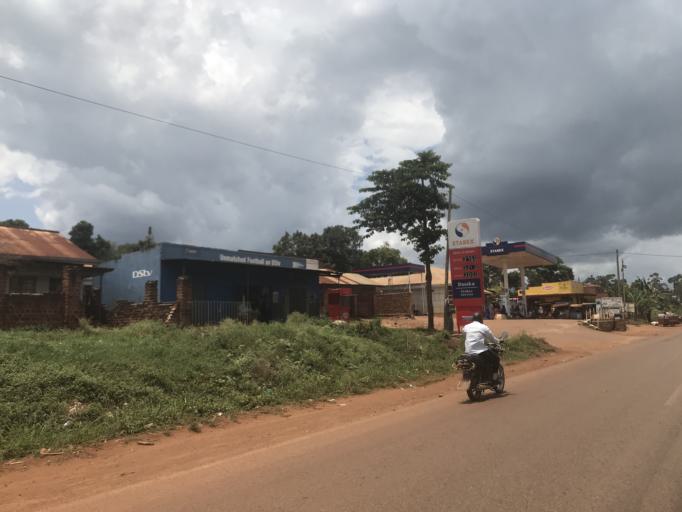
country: UG
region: Eastern Region
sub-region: Jinja District
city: Bugembe
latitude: 0.4724
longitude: 33.2547
